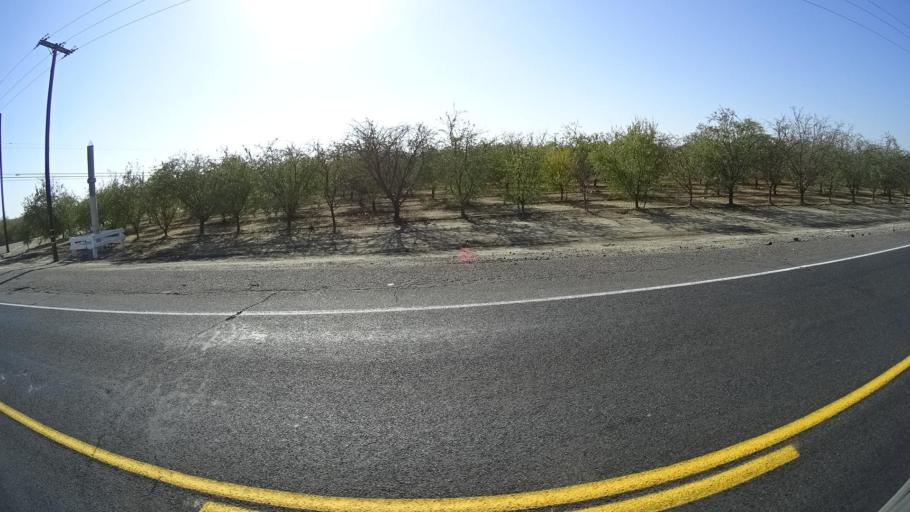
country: US
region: California
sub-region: Kern County
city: McFarland
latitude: 35.7179
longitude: -119.2413
